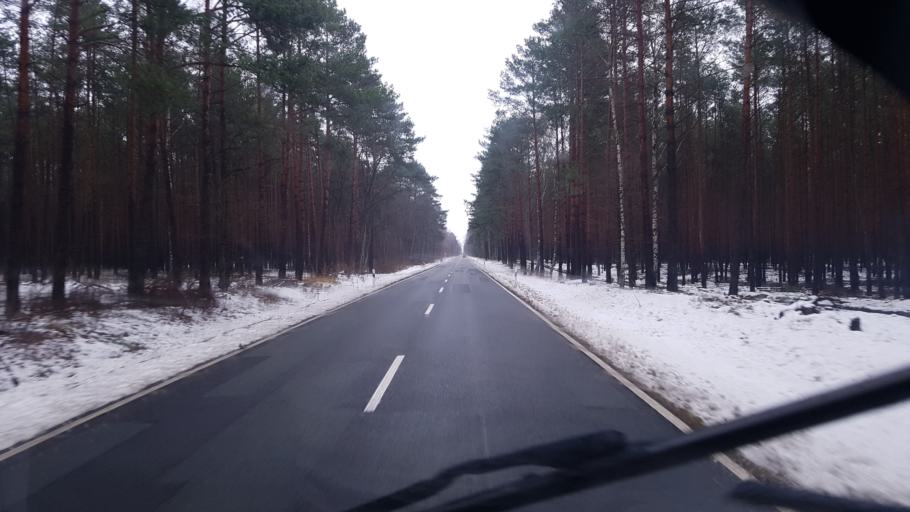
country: DE
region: Brandenburg
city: Tauer
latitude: 51.9813
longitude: 14.4632
